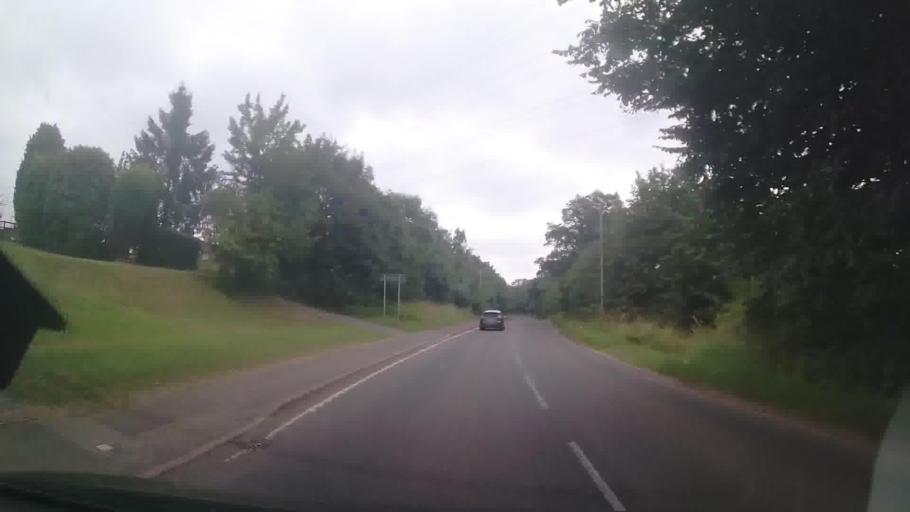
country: GB
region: England
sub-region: Leicestershire
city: Desford
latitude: 52.6429
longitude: -1.2869
